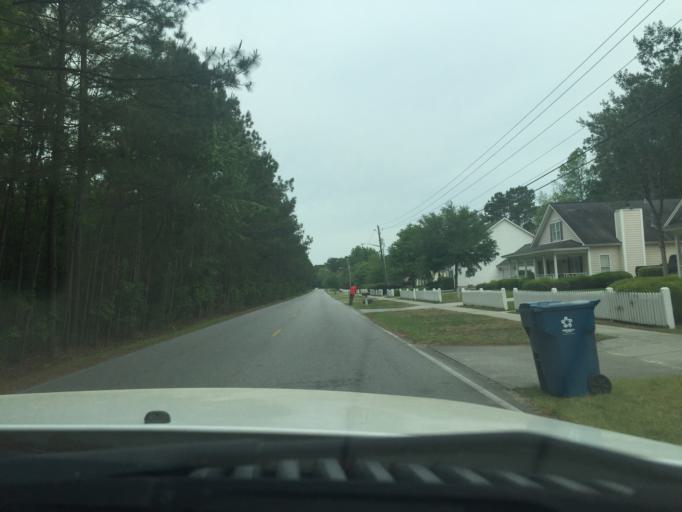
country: US
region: Georgia
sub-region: Chatham County
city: Georgetown
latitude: 31.9694
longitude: -81.2370
